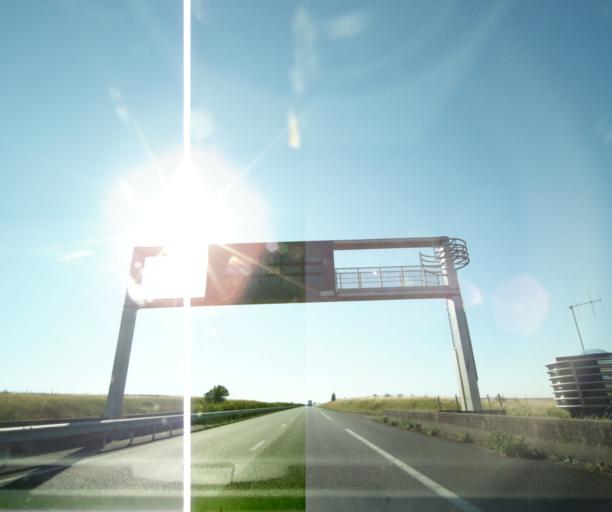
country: FR
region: Champagne-Ardenne
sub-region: Departement de l'Aube
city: Aix-en-Othe
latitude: 48.2436
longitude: 3.5684
